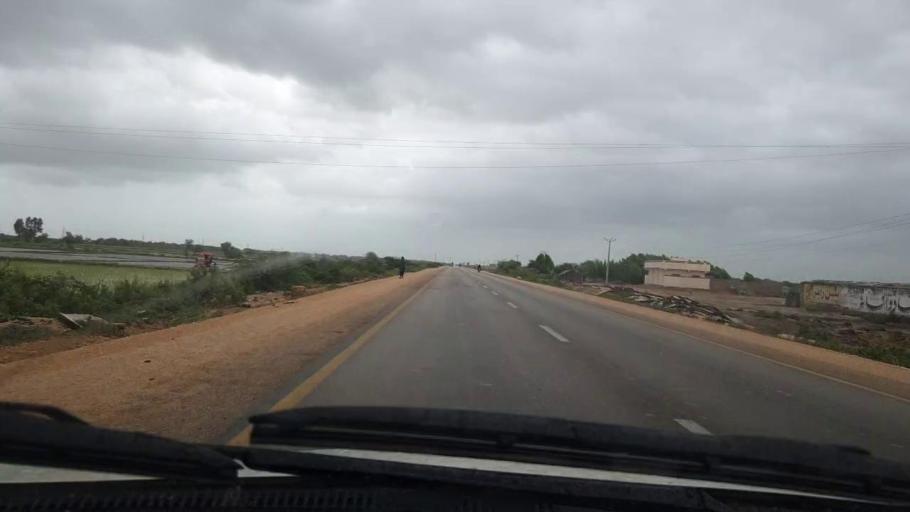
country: PK
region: Sindh
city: Badin
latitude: 24.6561
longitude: 68.7022
